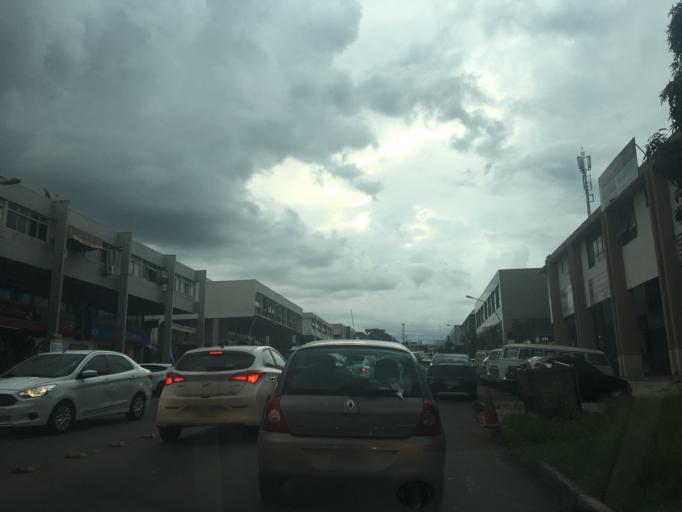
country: BR
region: Federal District
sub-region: Brasilia
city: Brasilia
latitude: -15.7437
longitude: -47.8940
